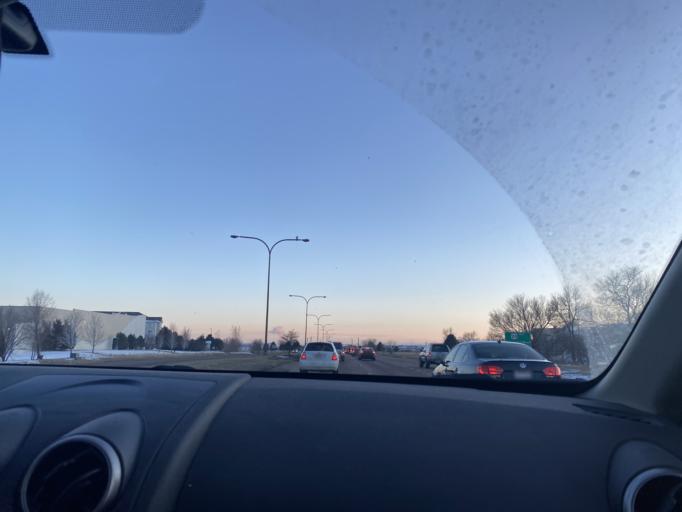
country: US
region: Colorado
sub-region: El Paso County
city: Cimarron Hills
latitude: 38.8106
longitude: -104.7304
